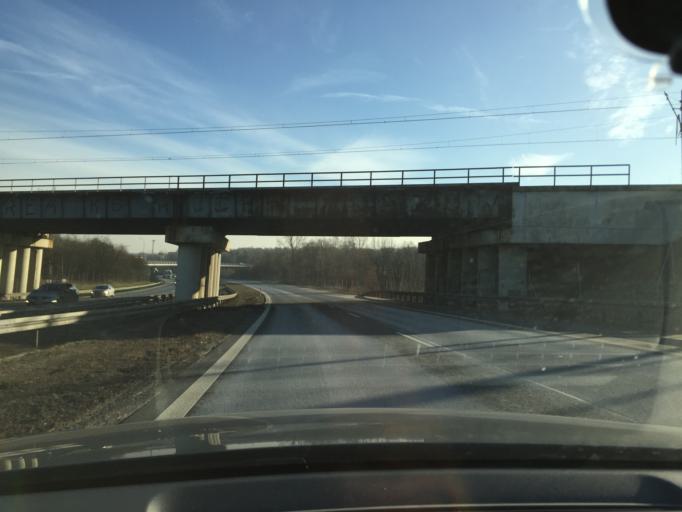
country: PL
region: Silesian Voivodeship
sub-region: Katowice
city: Murcki
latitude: 50.2322
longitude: 19.0645
